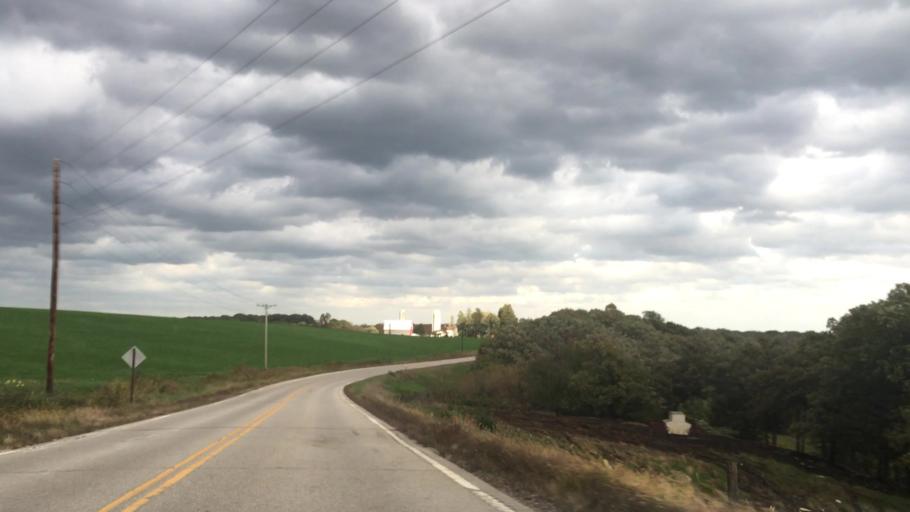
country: US
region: Minnesota
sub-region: Fillmore County
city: Preston
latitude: 43.7353
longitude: -92.0249
